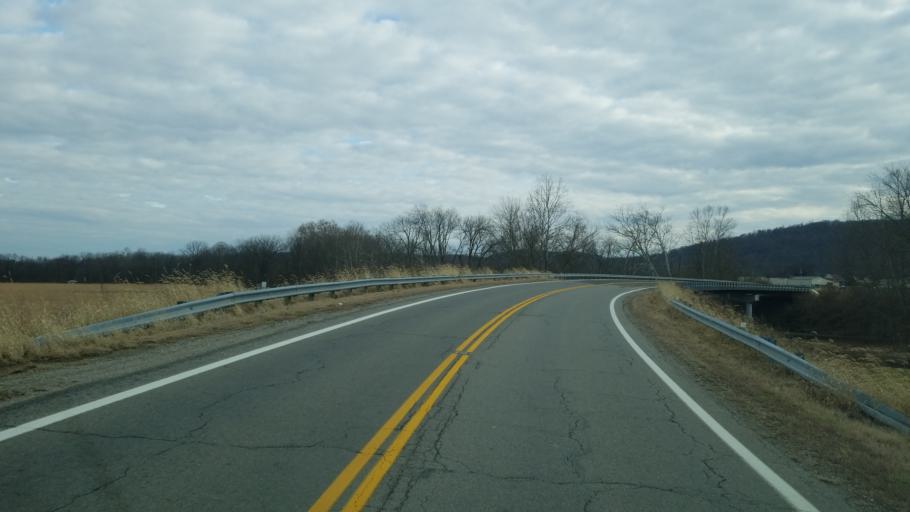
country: US
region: Ohio
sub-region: Highland County
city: Greenfield
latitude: 39.2361
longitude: -83.2737
